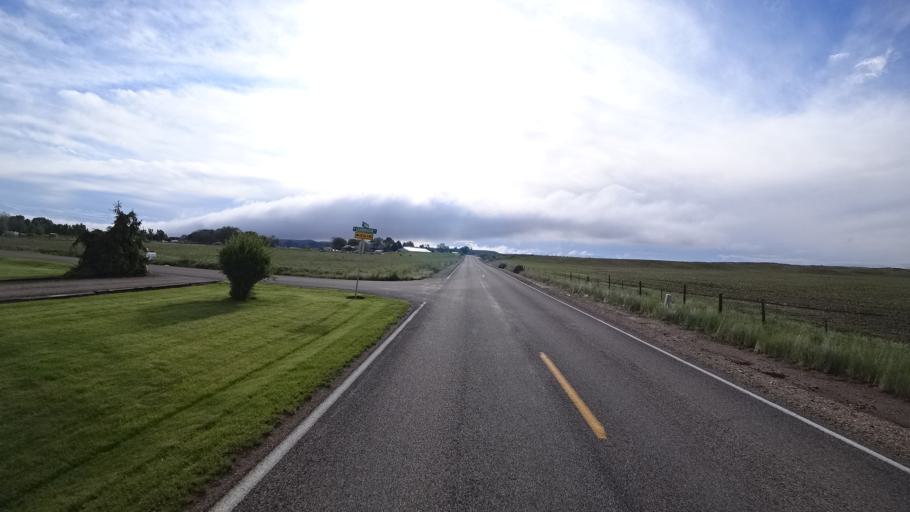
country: US
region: Idaho
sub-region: Ada County
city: Star
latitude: 43.7718
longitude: -116.4859
